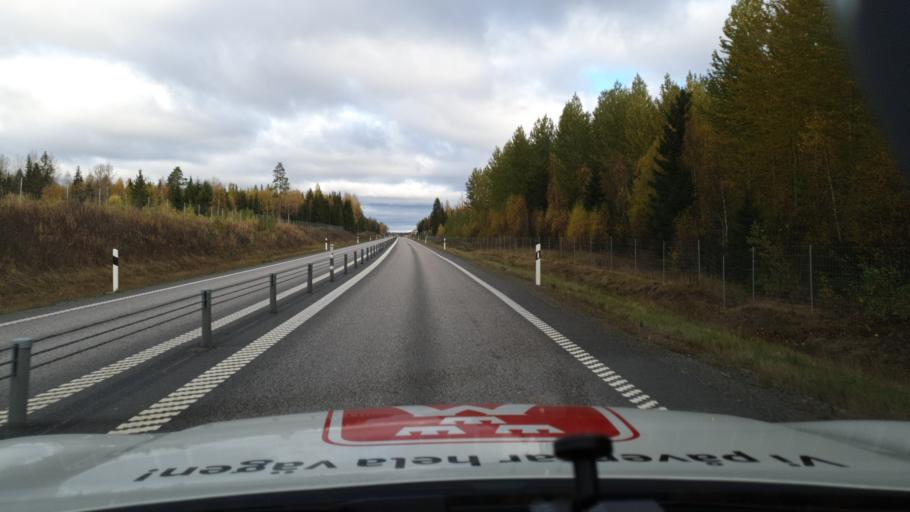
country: SE
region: Uppsala
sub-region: Heby Kommun
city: Heby
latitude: 59.9823
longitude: 16.8534
